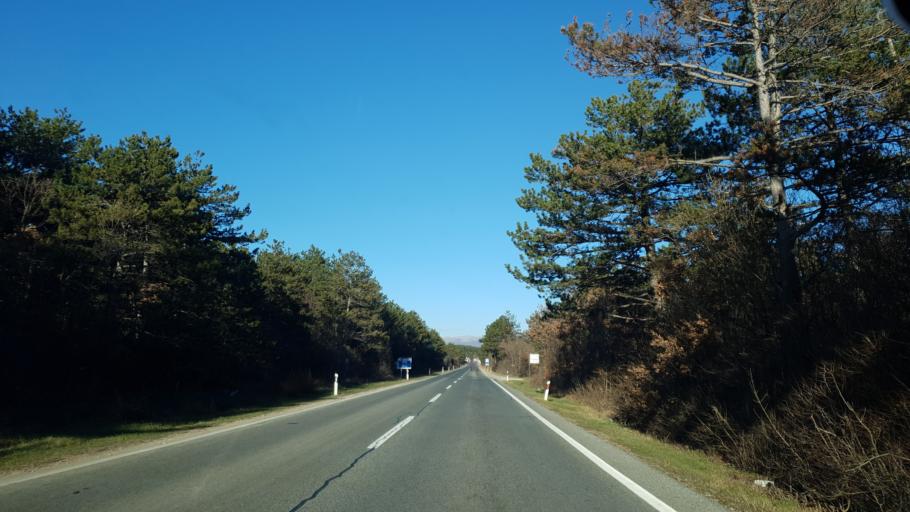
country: HR
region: Splitsko-Dalmatinska
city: Brnaze
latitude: 43.6563
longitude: 16.6408
